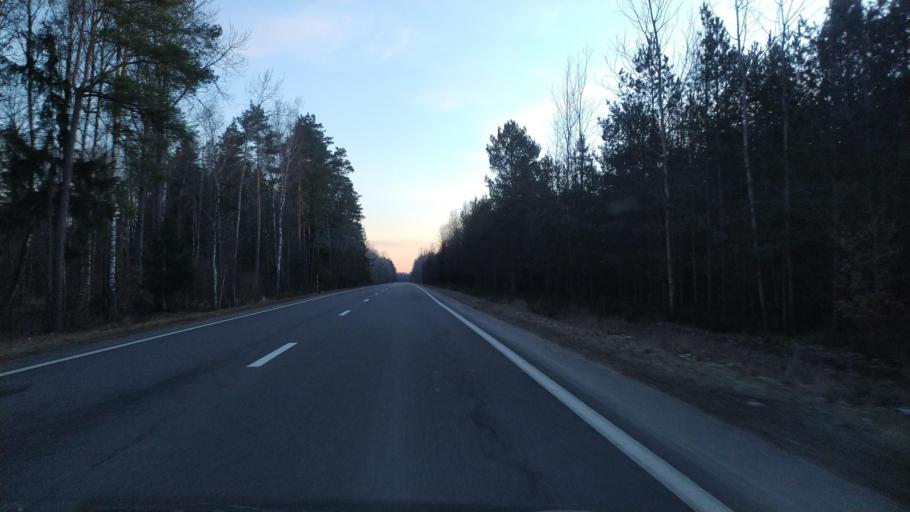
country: BY
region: Brest
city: Pruzhany
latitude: 52.5134
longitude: 24.1795
